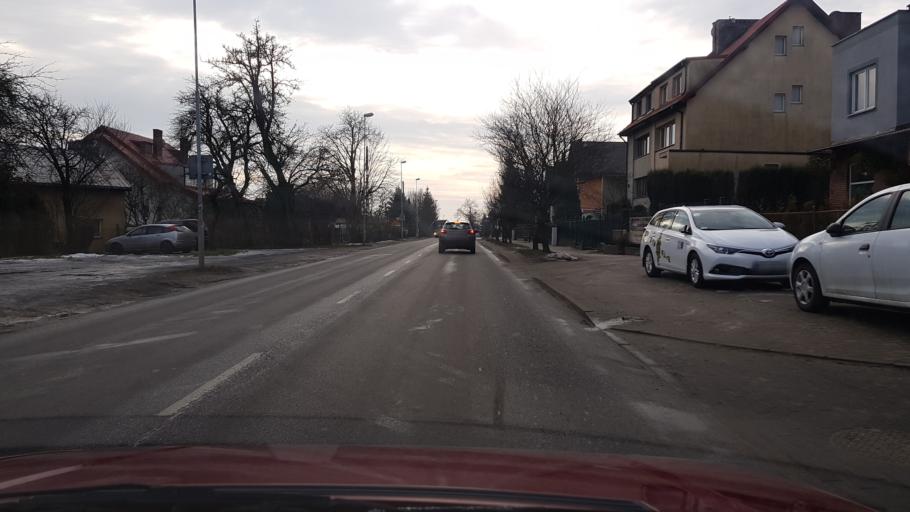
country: PL
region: West Pomeranian Voivodeship
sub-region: Szczecin
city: Szczecin
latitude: 53.4836
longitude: 14.5866
